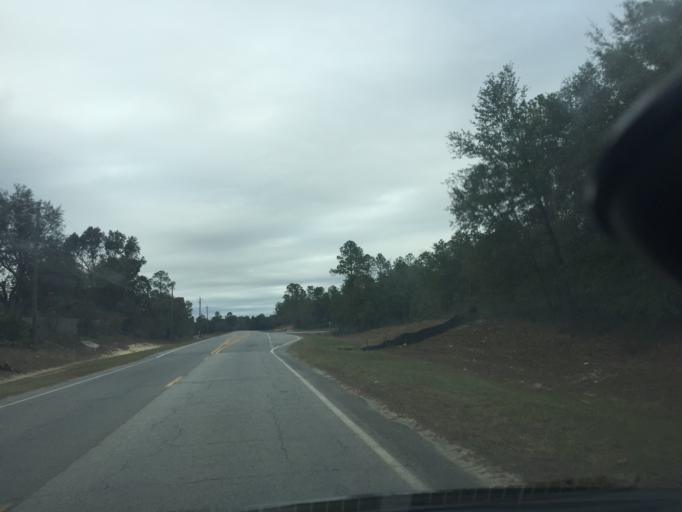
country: US
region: Georgia
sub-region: Chatham County
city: Bloomingdale
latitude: 32.1158
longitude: -81.3876
